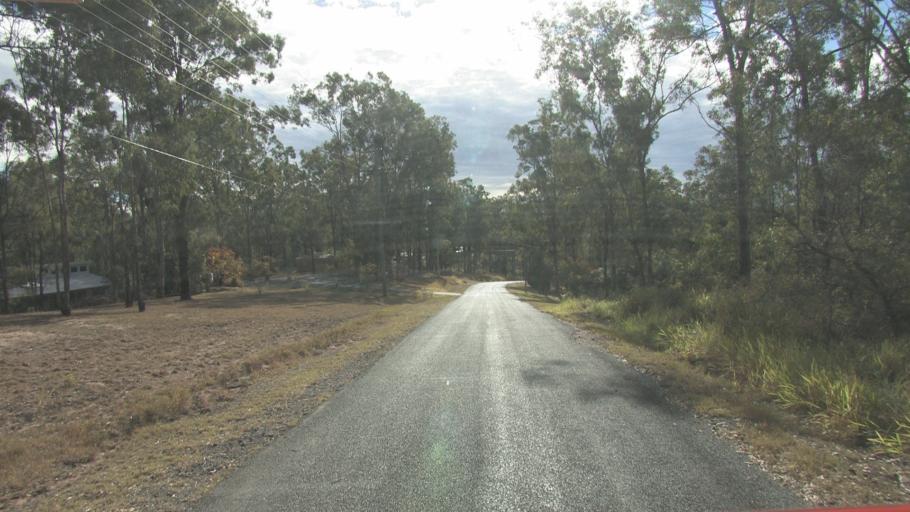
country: AU
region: Queensland
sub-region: Logan
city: Cedar Vale
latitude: -27.8443
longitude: 153.0703
